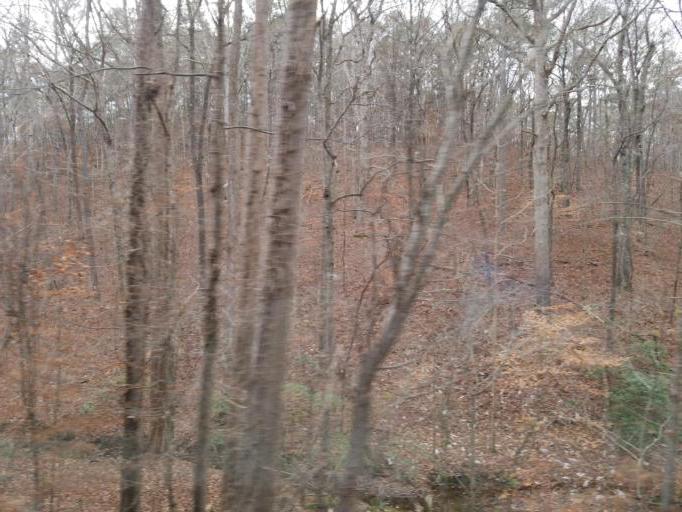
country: US
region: Georgia
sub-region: Cherokee County
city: Holly Springs
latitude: 34.2137
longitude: -84.5577
